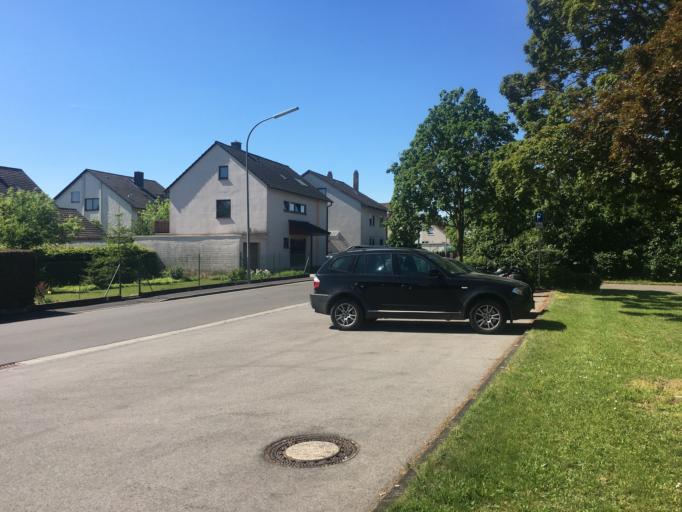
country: DE
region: Bavaria
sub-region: Regierungsbezirk Unterfranken
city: Bergrheinfeld
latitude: 50.0132
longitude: 10.1819
